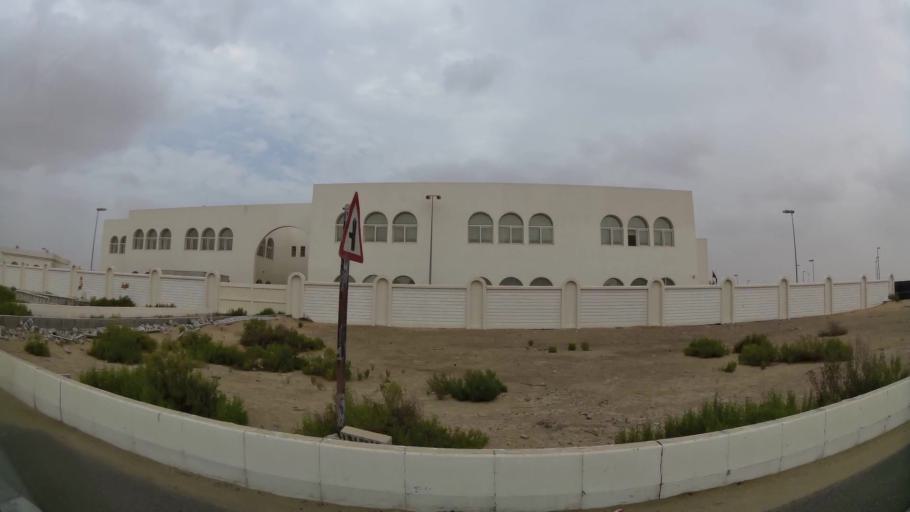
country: AE
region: Abu Dhabi
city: Abu Dhabi
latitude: 24.3488
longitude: 54.6489
